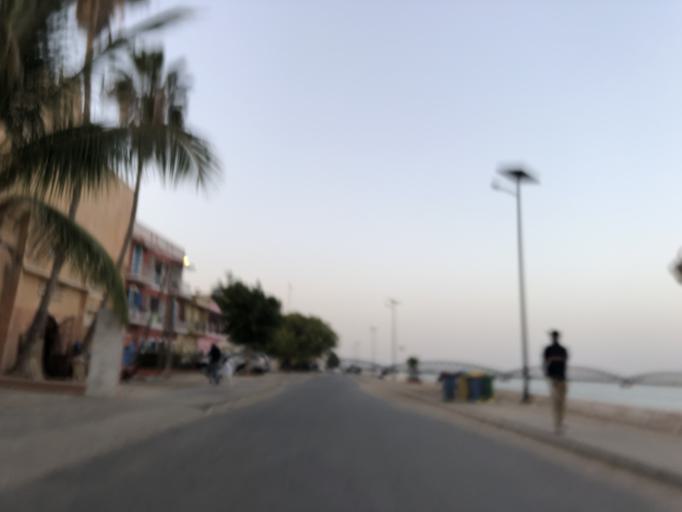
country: SN
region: Saint-Louis
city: Saint-Louis
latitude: 16.0229
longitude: -16.5040
